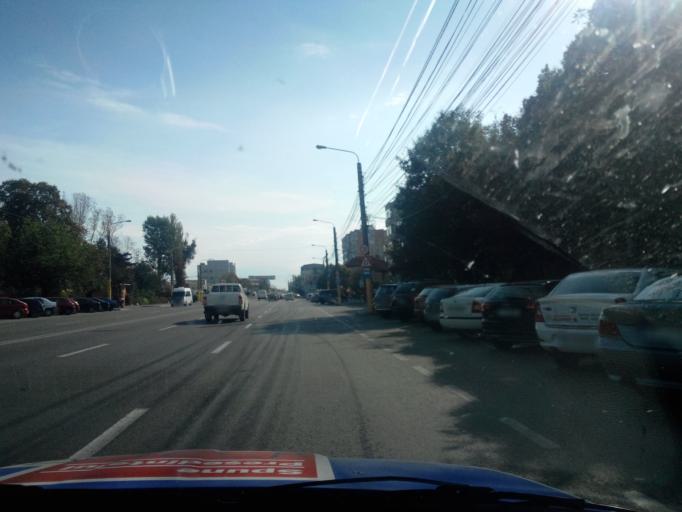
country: RO
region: Constanta
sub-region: Municipiul Constanta
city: Constanta
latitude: 44.1578
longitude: 28.6127
